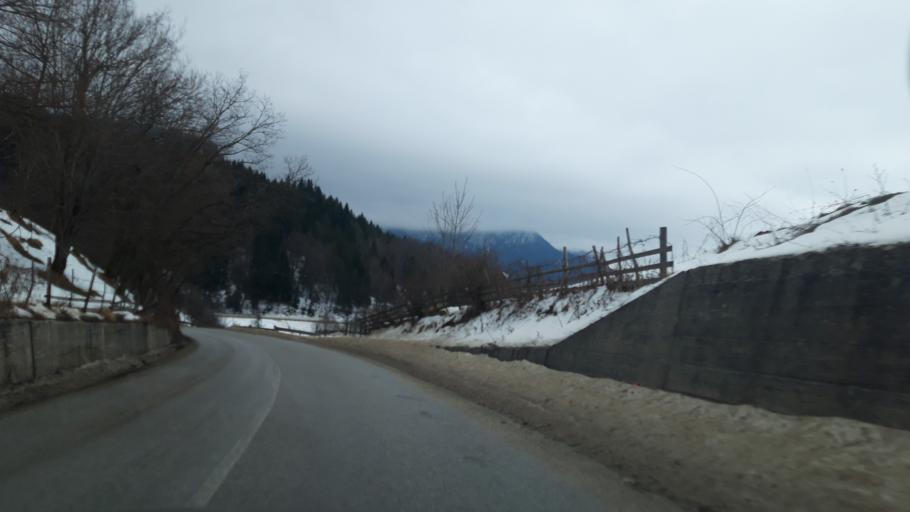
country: BA
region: Republika Srpska
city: Pale
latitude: 43.9045
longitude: 18.6365
